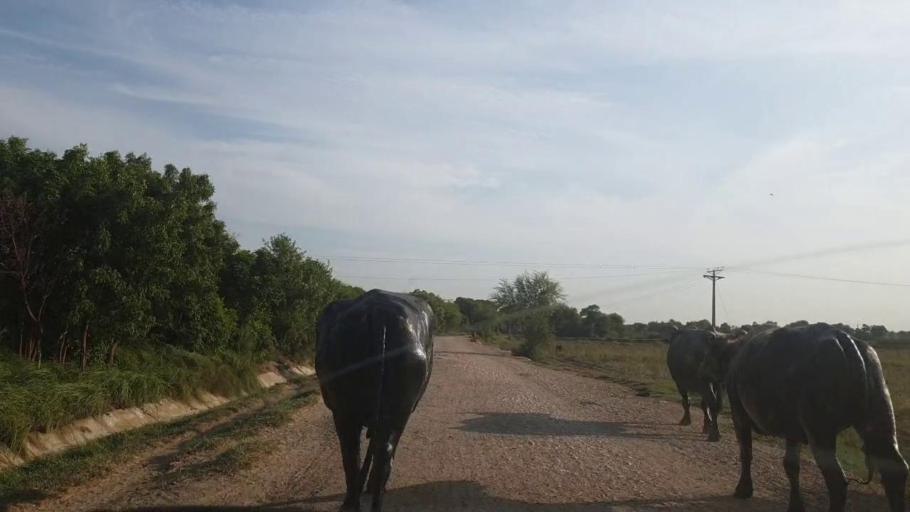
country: PK
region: Sindh
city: Tando Muhammad Khan
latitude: 25.2234
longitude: 68.5375
